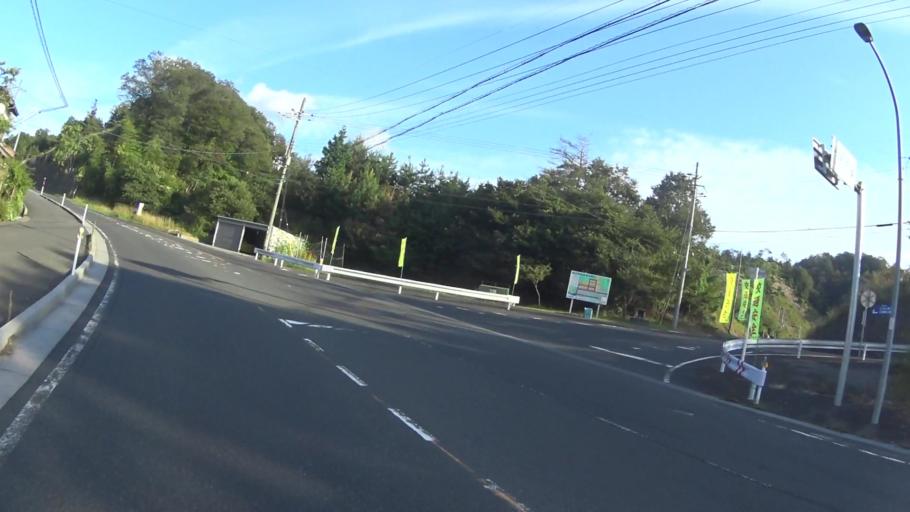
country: JP
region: Hyogo
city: Toyooka
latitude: 35.5841
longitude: 134.9539
